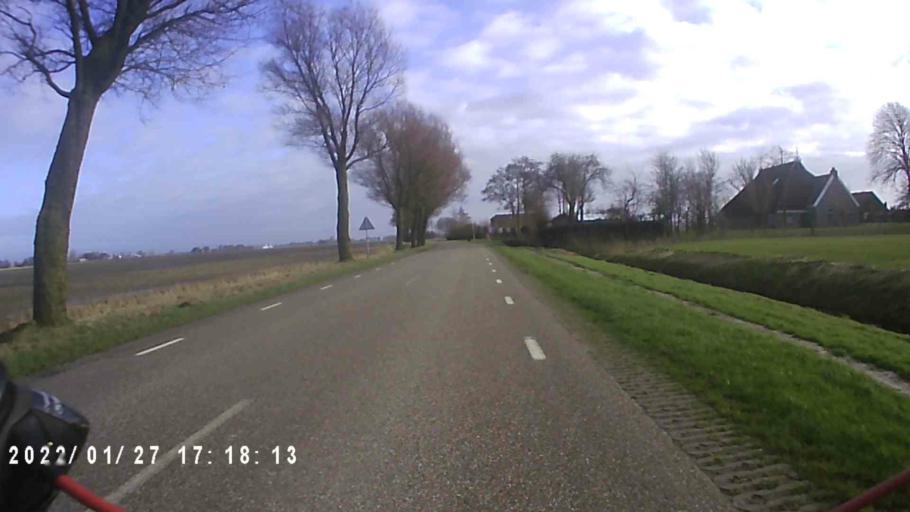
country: NL
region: Friesland
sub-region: Gemeente Dongeradeel
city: Anjum
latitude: 53.3896
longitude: 6.1045
